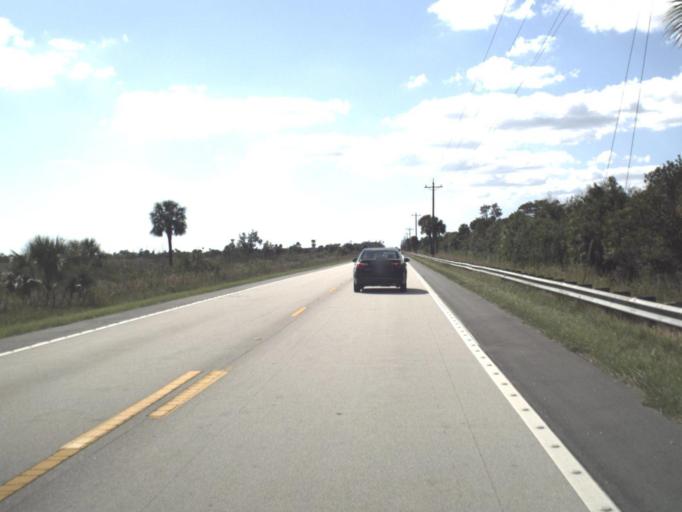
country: US
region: Florida
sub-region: Collier County
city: Marco
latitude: 25.9015
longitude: -81.3125
